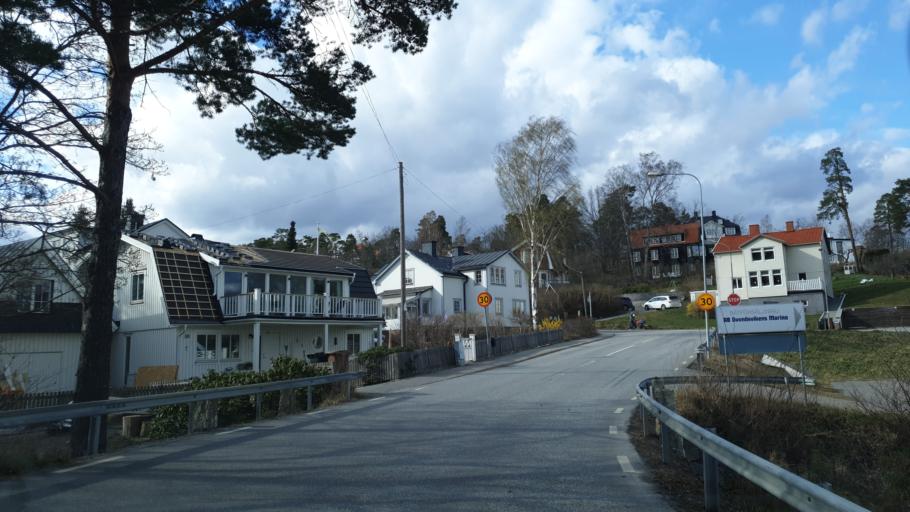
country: SE
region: Stockholm
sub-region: Nacka Kommun
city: Alta
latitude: 59.3003
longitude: 18.2023
